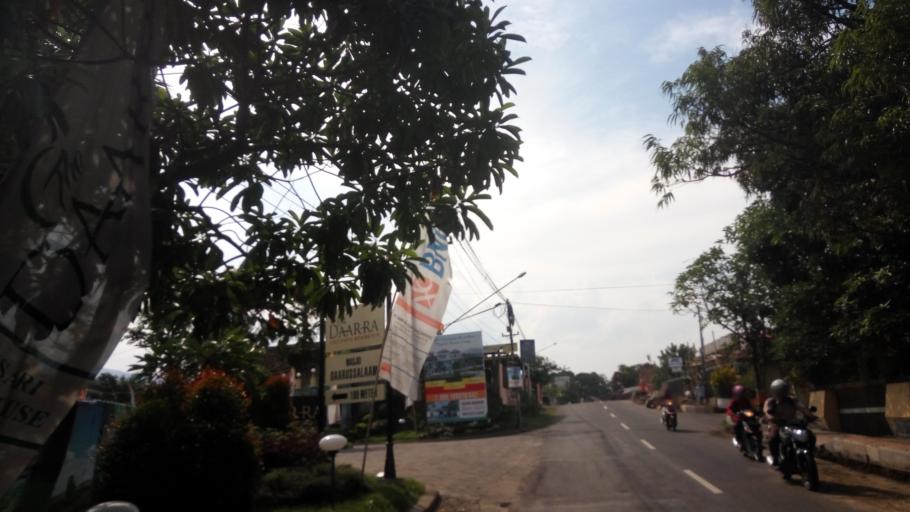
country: ID
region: Central Java
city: Ungaran
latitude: -7.1307
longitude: 110.4172
